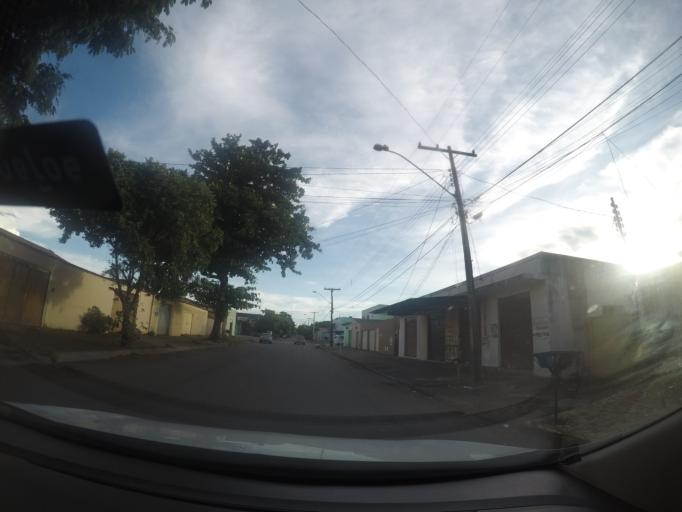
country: BR
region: Goias
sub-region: Goiania
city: Goiania
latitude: -16.6807
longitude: -49.3179
